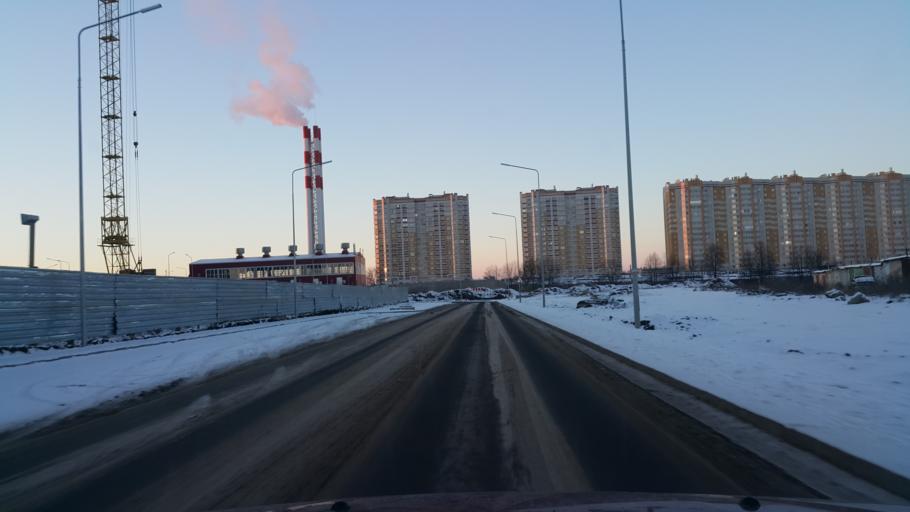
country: RU
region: Tambov
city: Tambov
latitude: 52.7592
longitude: 41.3954
